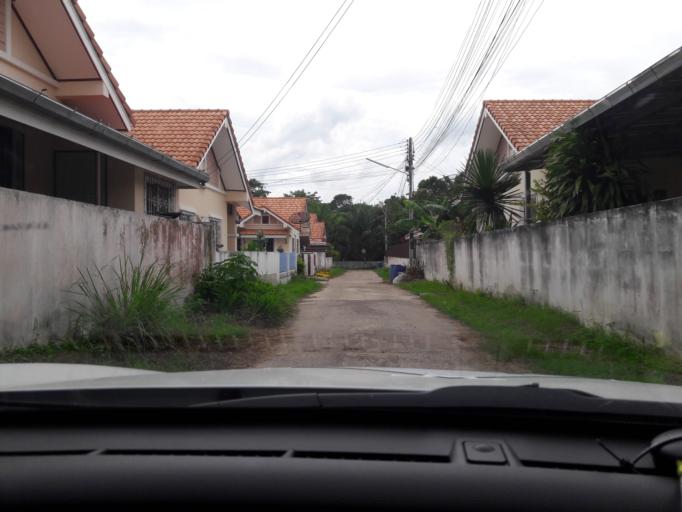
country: TH
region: Nakhon Sawan
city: Tak Fa
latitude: 15.3441
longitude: 100.5029
